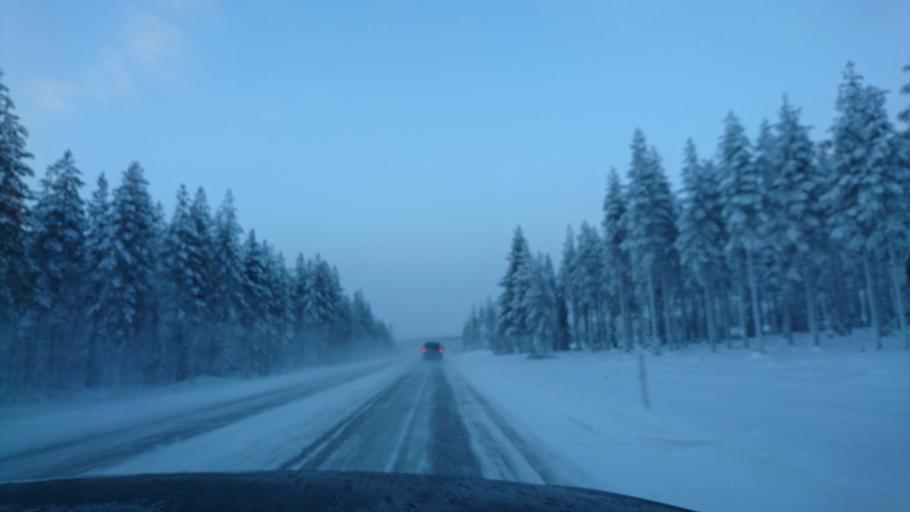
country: FI
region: Northern Ostrobothnia
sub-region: Koillismaa
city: Taivalkoski
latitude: 65.4762
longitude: 27.7726
